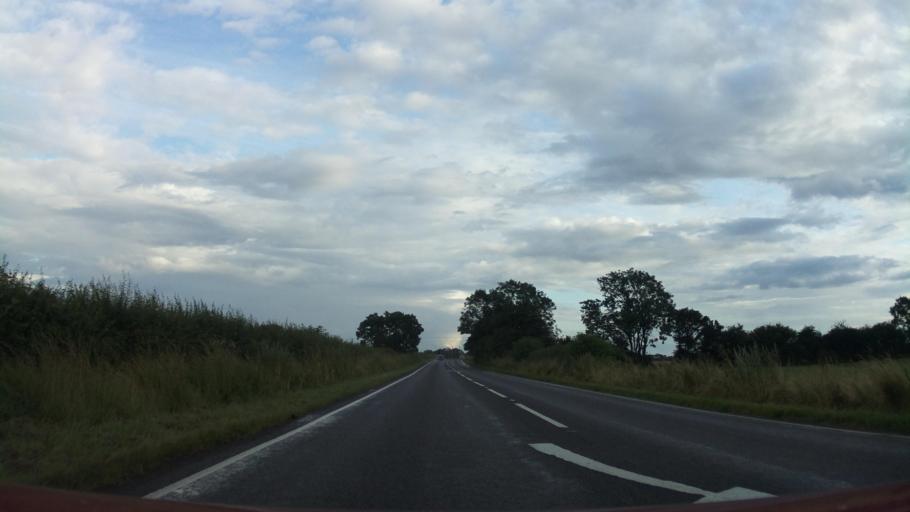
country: GB
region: England
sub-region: Oxfordshire
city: Woodstock
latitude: 51.8778
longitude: -1.3293
